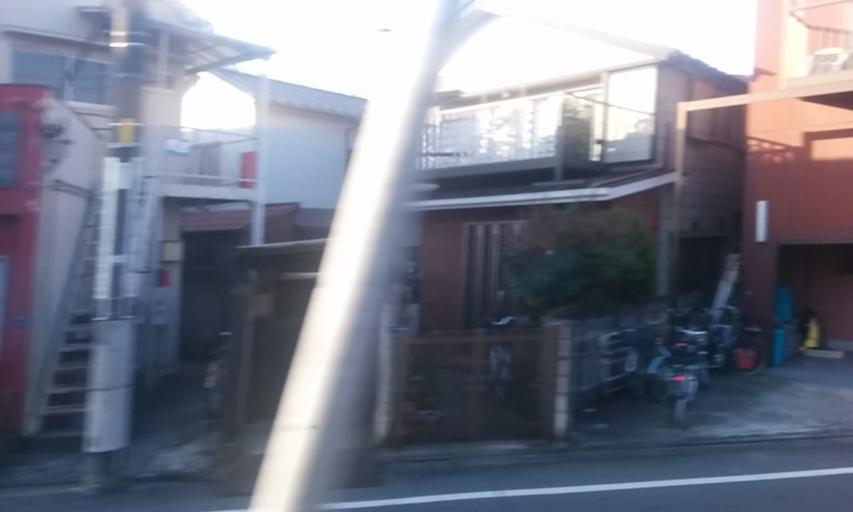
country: JP
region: Saitama
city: Shimotoda
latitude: 35.7621
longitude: 139.6798
